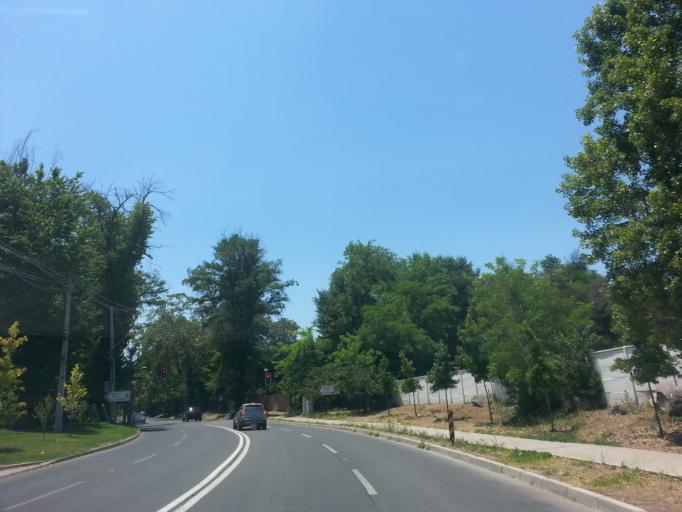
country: CL
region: Santiago Metropolitan
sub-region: Provincia de Santiago
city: Villa Presidente Frei, Nunoa, Santiago, Chile
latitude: -33.3855
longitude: -70.5292
